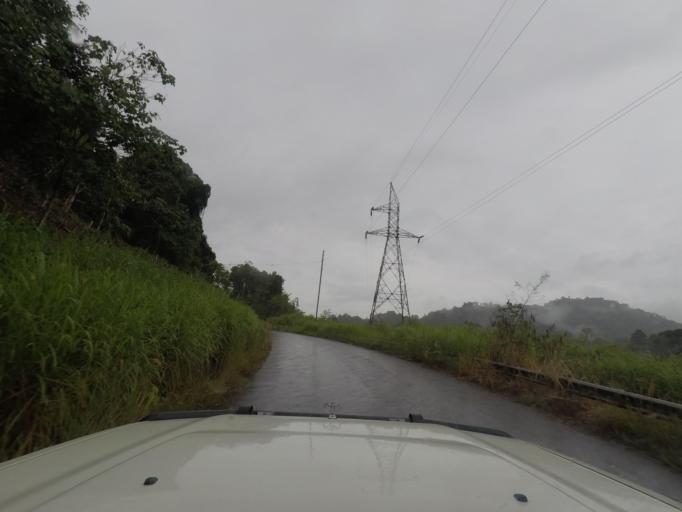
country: PG
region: Madang
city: Madang
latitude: -5.4107
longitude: 145.5658
